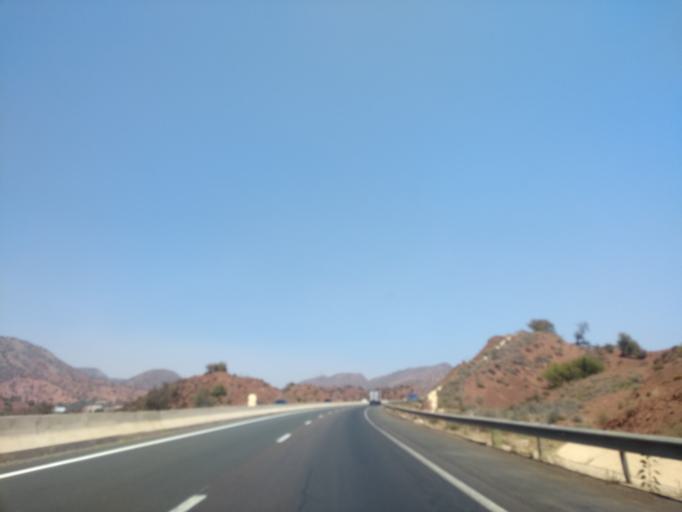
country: MA
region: Souss-Massa-Draa
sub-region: Taroudannt
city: Bigoudine
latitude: 30.6269
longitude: -9.3336
